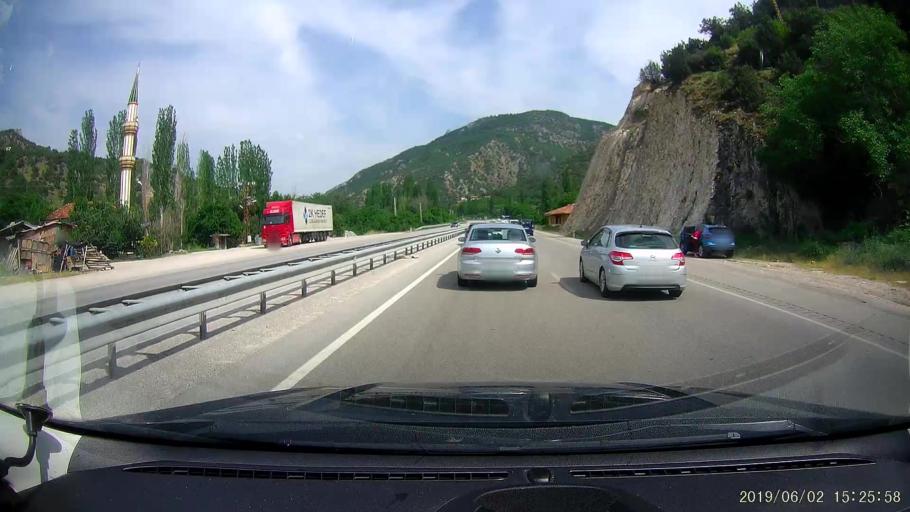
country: TR
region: Amasya
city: Saraycik
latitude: 40.9892
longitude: 35.0290
